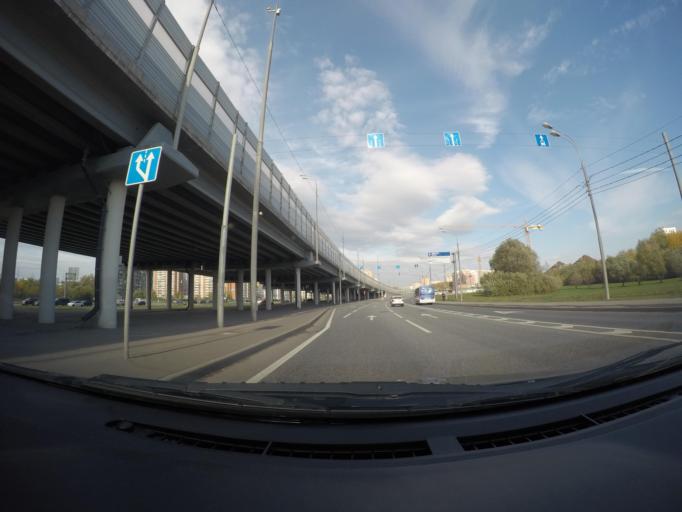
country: RU
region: Moscow
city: Severnyy
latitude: 55.9186
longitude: 37.5447
